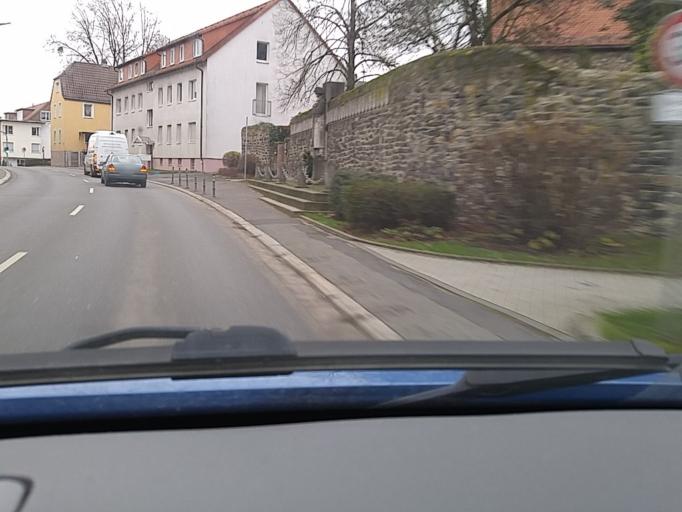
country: DE
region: Hesse
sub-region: Regierungsbezirk Darmstadt
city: Friedberg
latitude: 50.3290
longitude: 8.7710
